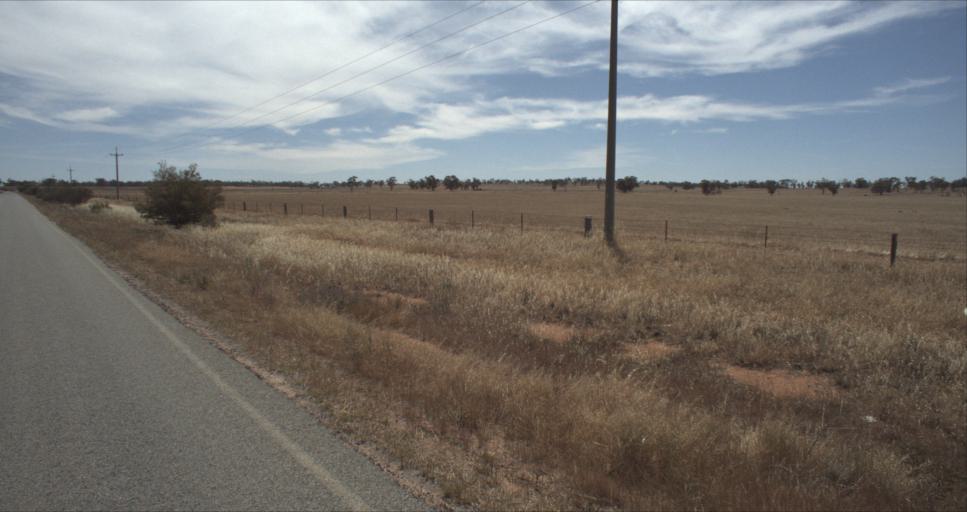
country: AU
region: New South Wales
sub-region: Leeton
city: Leeton
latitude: -34.6264
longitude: 146.4518
